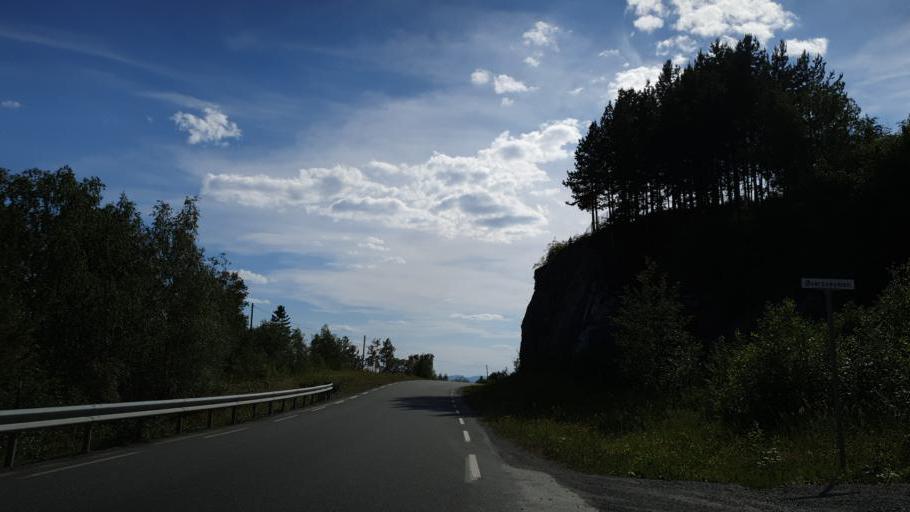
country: NO
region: Nord-Trondelag
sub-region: Leksvik
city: Leksvik
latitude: 63.6219
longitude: 10.5292
